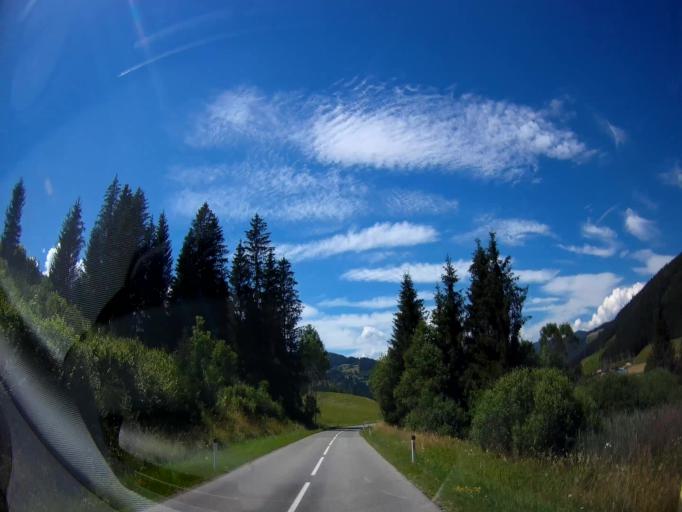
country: AT
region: Carinthia
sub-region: Politischer Bezirk Sankt Veit an der Glan
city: Glodnitz
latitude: 46.8648
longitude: 14.1261
